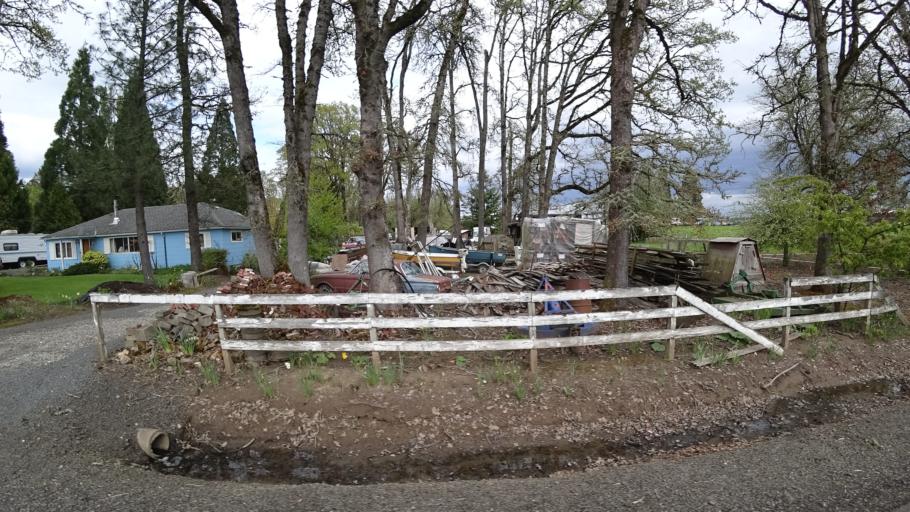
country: US
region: Oregon
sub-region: Washington County
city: Hillsboro
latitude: 45.5527
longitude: -122.9528
